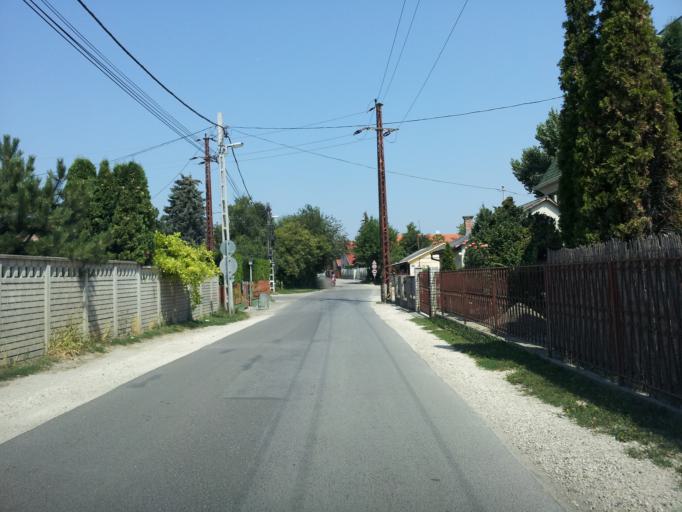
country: HU
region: Pest
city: Szigetszentmiklos
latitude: 47.3302
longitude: 19.0455
